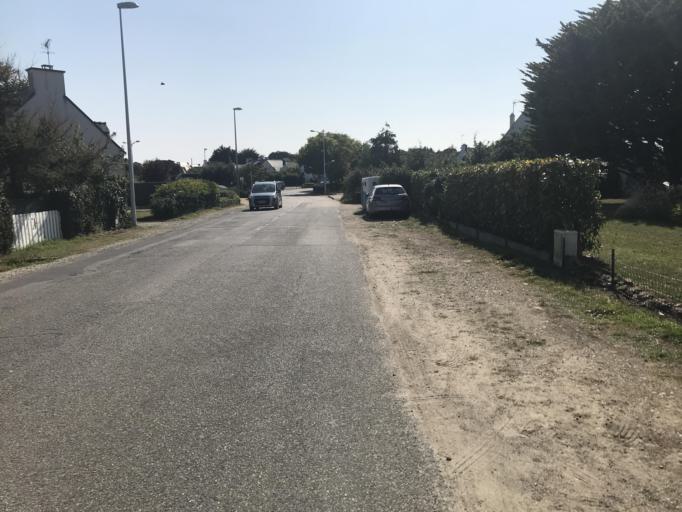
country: FR
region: Brittany
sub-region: Departement du Morbihan
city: Arzon
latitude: 47.5472
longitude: -2.9028
